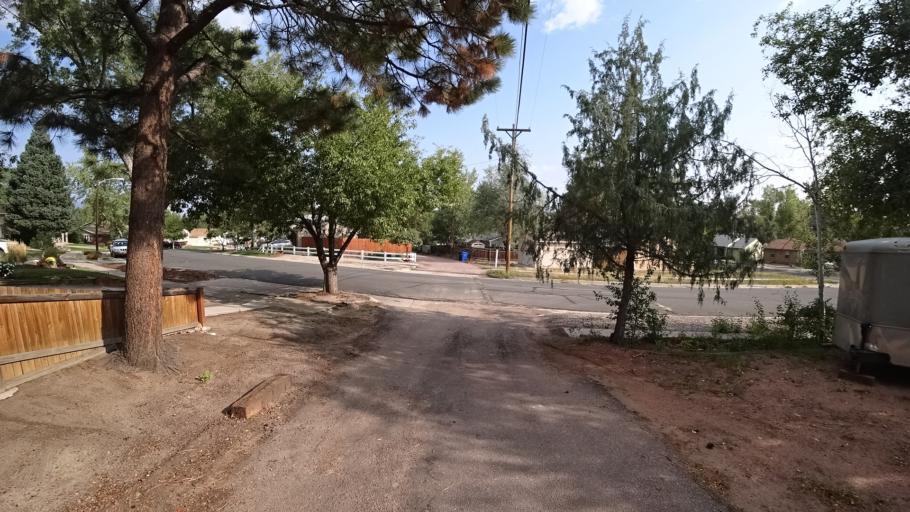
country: US
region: Colorado
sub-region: El Paso County
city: Colorado Springs
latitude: 38.8523
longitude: -104.7861
